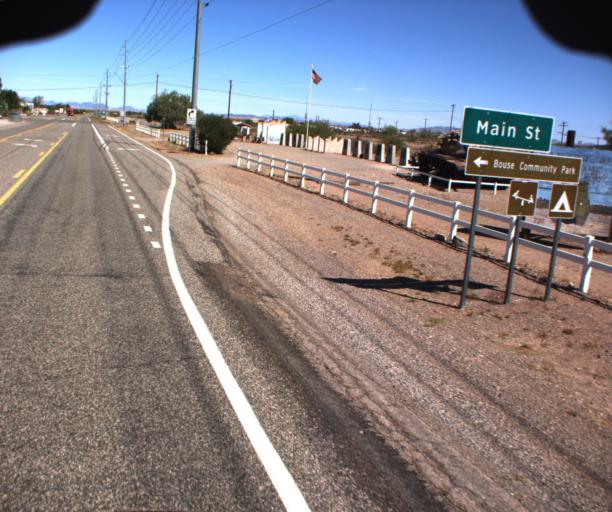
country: US
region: Arizona
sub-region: La Paz County
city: Cienega Springs
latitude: 33.9311
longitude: -114.0048
